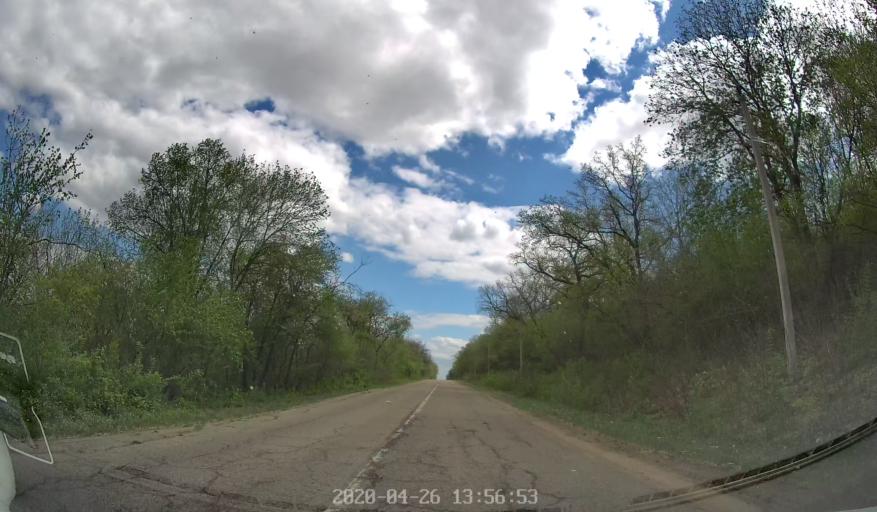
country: MD
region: Telenesti
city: Cocieri
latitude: 47.2776
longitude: 29.1111
